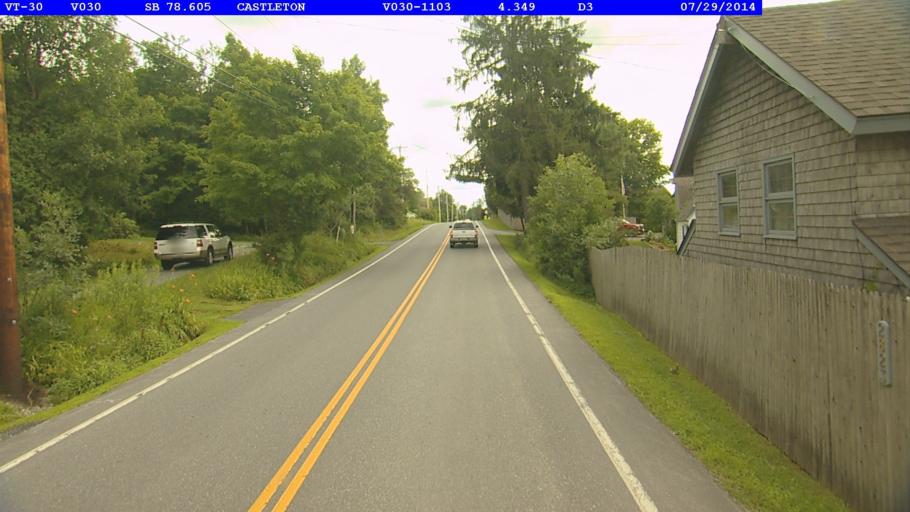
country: US
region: Vermont
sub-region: Rutland County
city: Castleton
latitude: 43.6483
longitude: -73.1962
